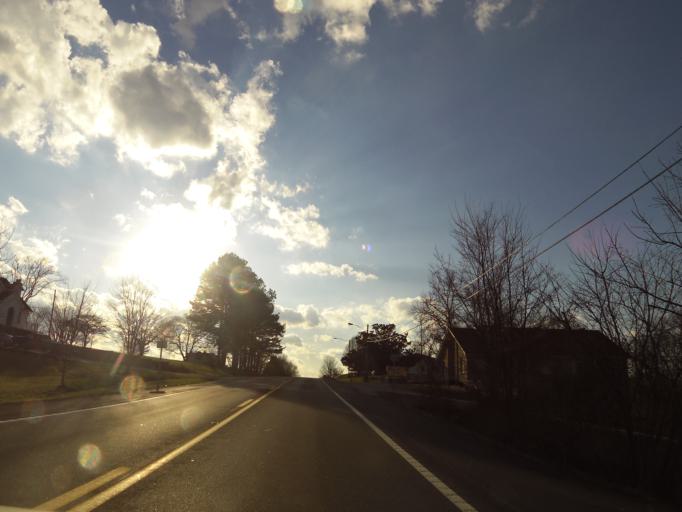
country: US
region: Tennessee
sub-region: Smith County
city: Carthage
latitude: 36.2582
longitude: -85.9797
